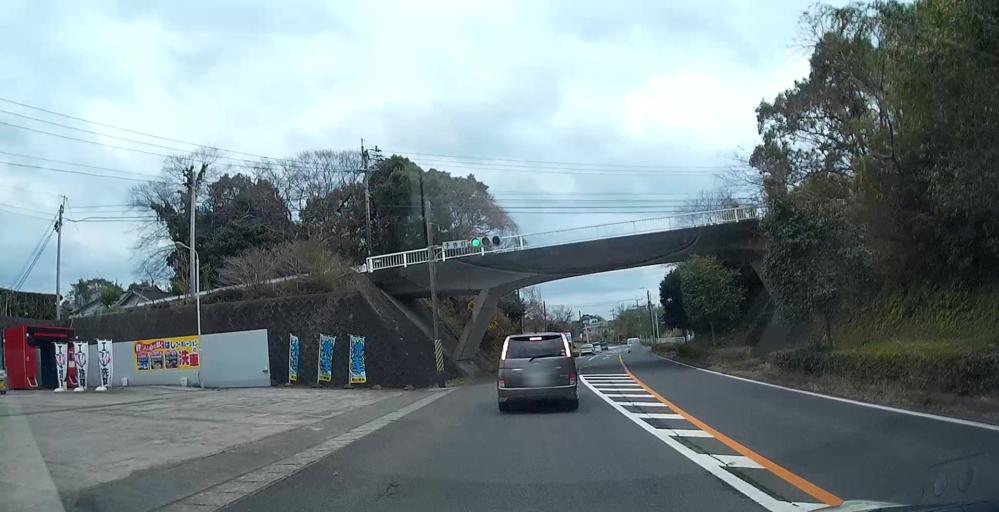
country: JP
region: Kagoshima
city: Akune
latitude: 32.0799
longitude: 130.2049
